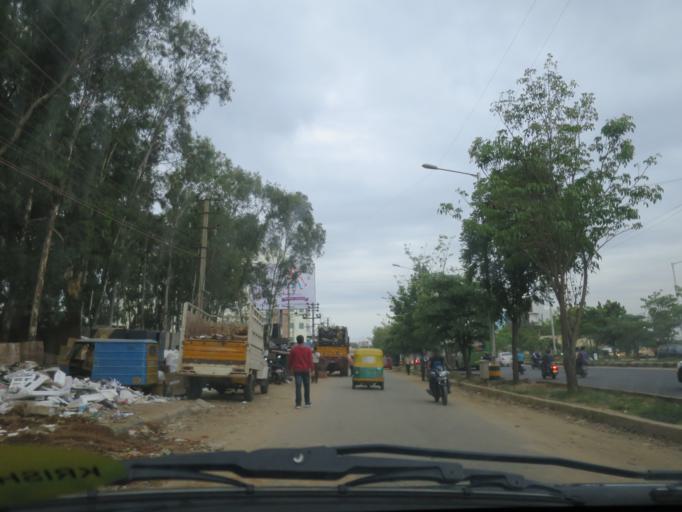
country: IN
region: Karnataka
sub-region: Bangalore Urban
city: Bangalore
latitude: 12.9764
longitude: 77.6969
